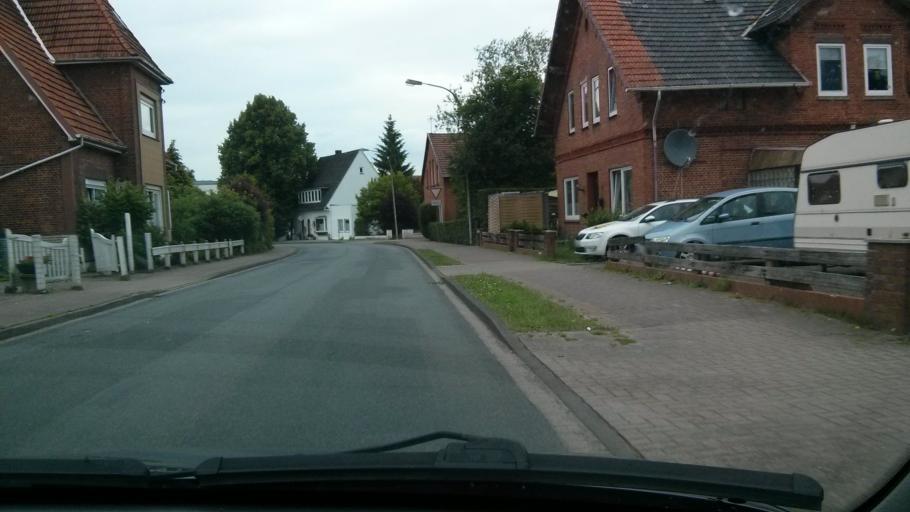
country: DE
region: Lower Saxony
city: Loxstedt
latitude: 53.4691
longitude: 8.6506
